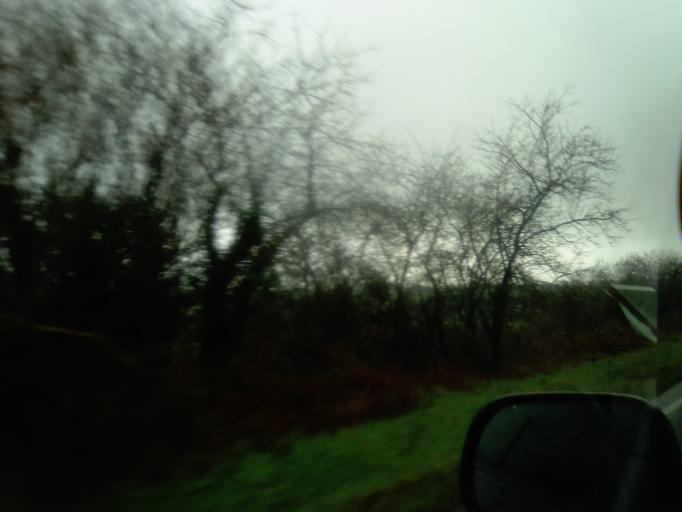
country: GB
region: Northern Ireland
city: Newtownstewart
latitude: 54.7114
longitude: -7.3603
